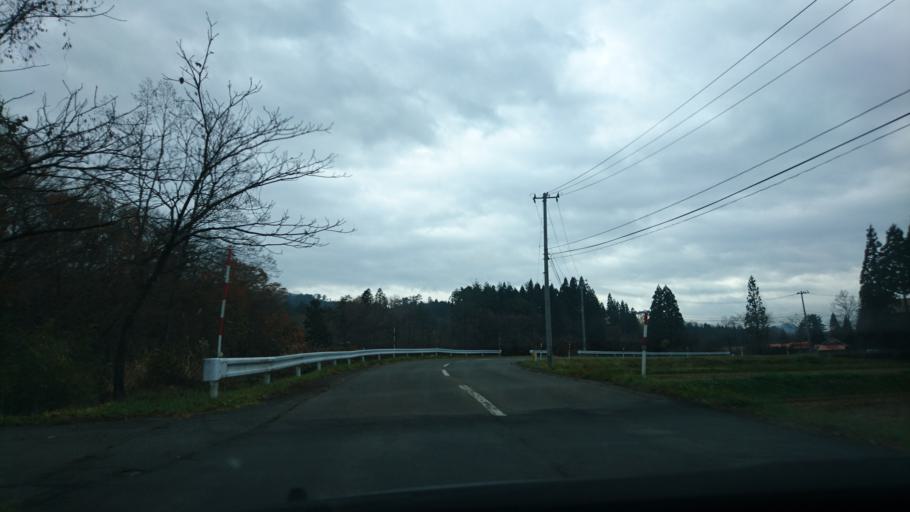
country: JP
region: Iwate
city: Ichinoseki
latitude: 38.9476
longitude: 140.9269
